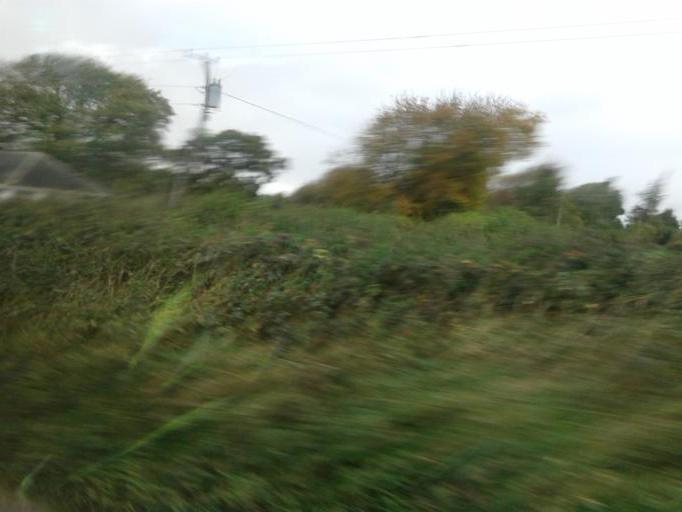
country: IE
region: Leinster
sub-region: Uibh Fhaili
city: Birr
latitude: 52.9583
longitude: -8.0207
